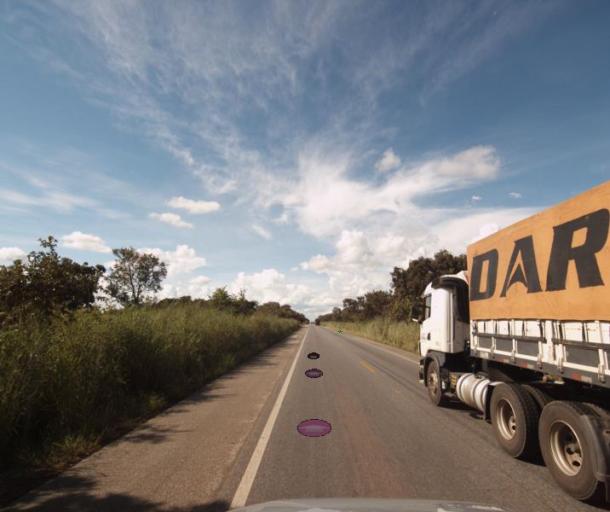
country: BR
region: Goias
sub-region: Porangatu
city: Porangatu
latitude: -12.9943
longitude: -49.1541
